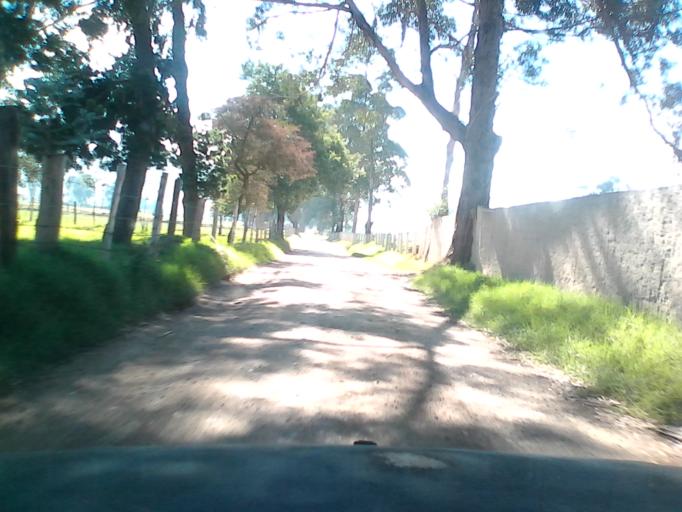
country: CO
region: Boyaca
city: Duitama
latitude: 5.7863
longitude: -73.0471
